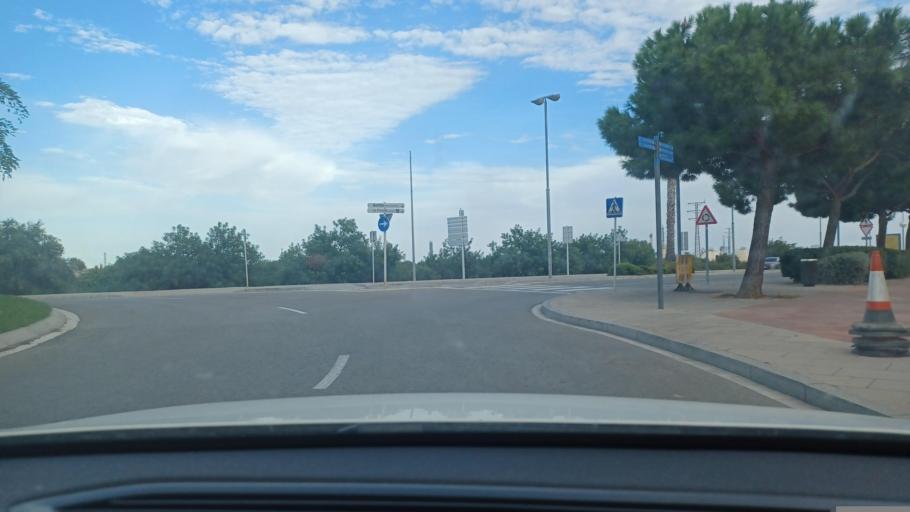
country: ES
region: Catalonia
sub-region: Provincia de Tarragona
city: Vila-seca
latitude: 41.1062
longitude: 1.1529
